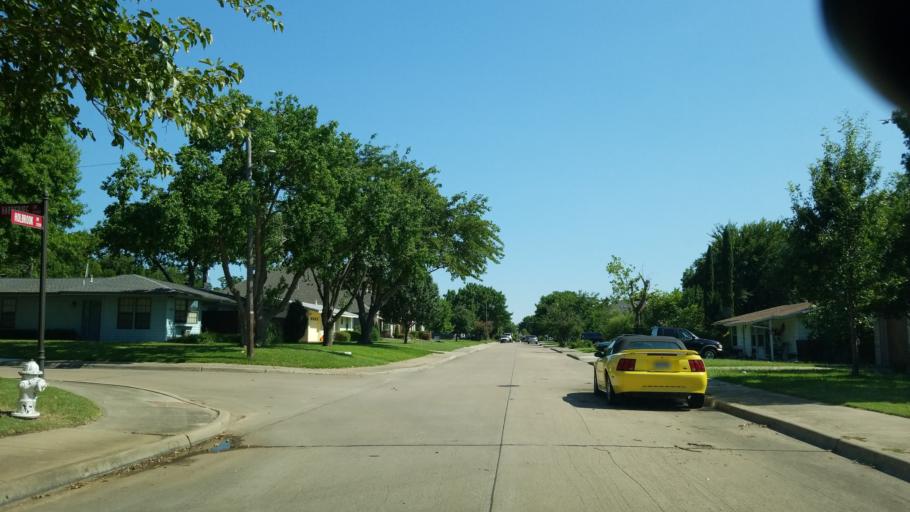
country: US
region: Texas
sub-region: Dallas County
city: Farmers Branch
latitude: 32.9238
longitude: -96.8869
